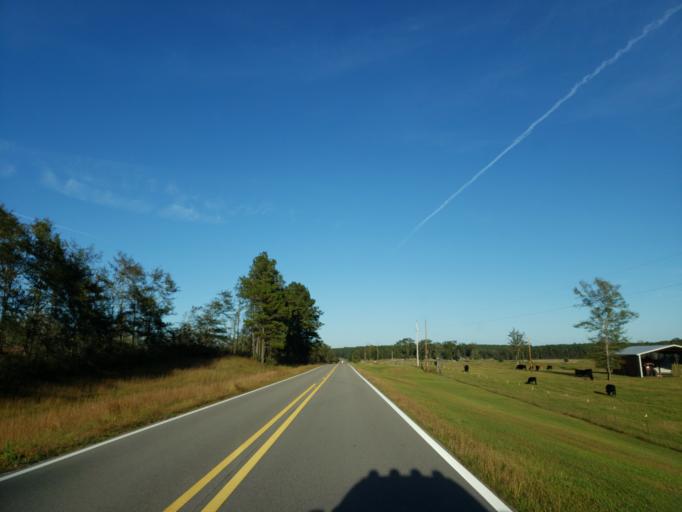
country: US
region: Mississippi
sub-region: Perry County
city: Richton
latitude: 31.3620
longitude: -88.7281
